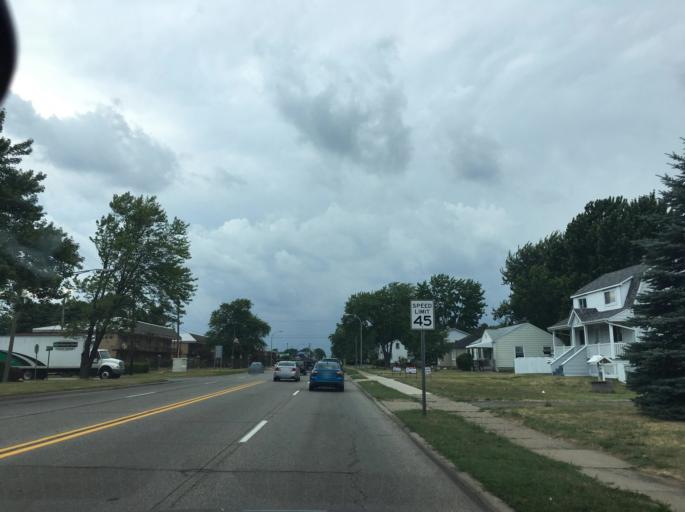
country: US
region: Michigan
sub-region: Macomb County
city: Roseville
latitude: 42.5101
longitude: -82.9199
